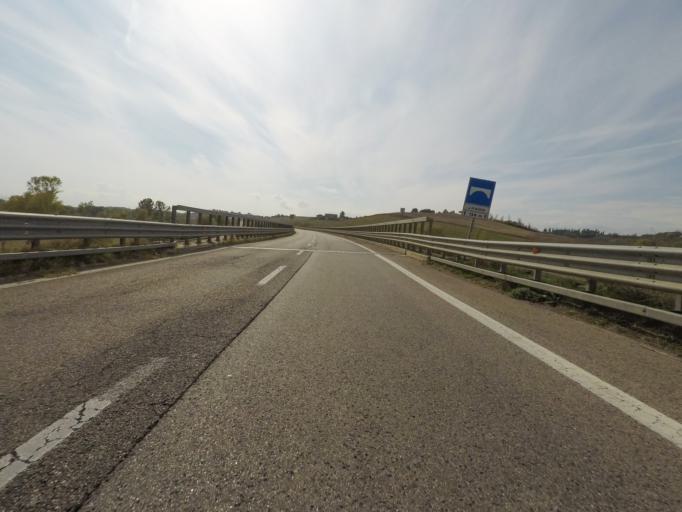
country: IT
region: Tuscany
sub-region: Provincia di Siena
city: Siena
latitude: 43.2851
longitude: 11.3323
